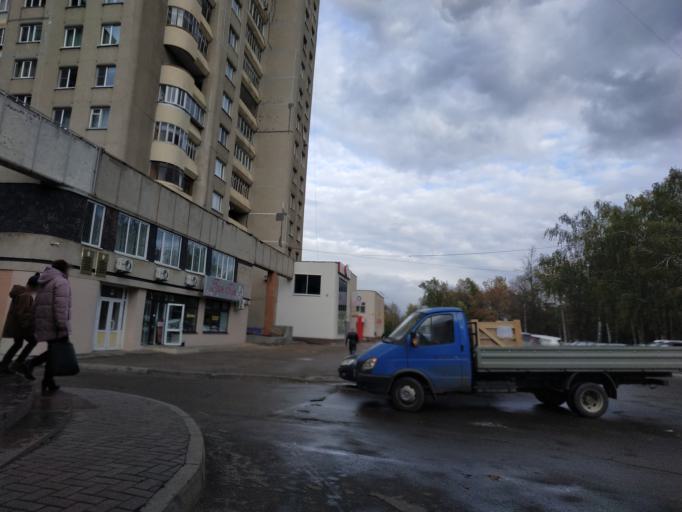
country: RU
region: Chuvashia
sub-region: Cheboksarskiy Rayon
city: Cheboksary
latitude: 56.1462
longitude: 47.2168
